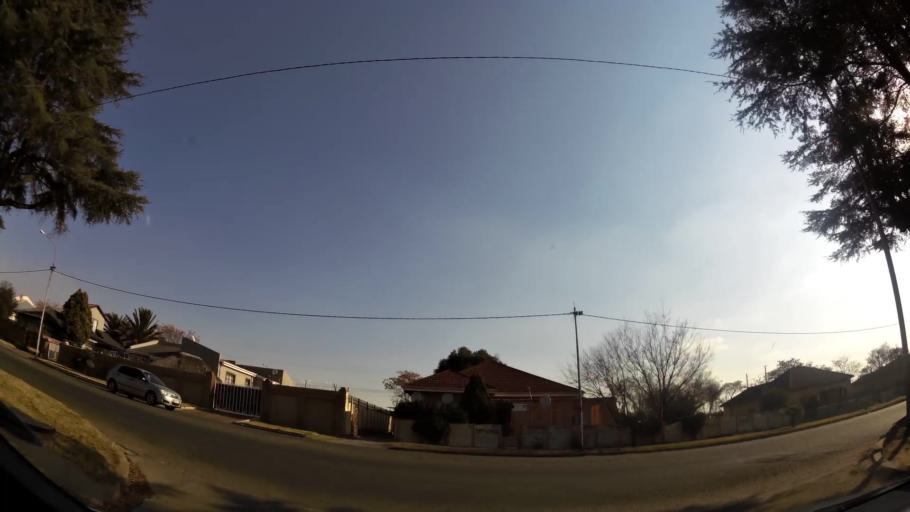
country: ZA
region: Gauteng
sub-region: Ekurhuleni Metropolitan Municipality
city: Brakpan
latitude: -26.2350
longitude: 28.3591
